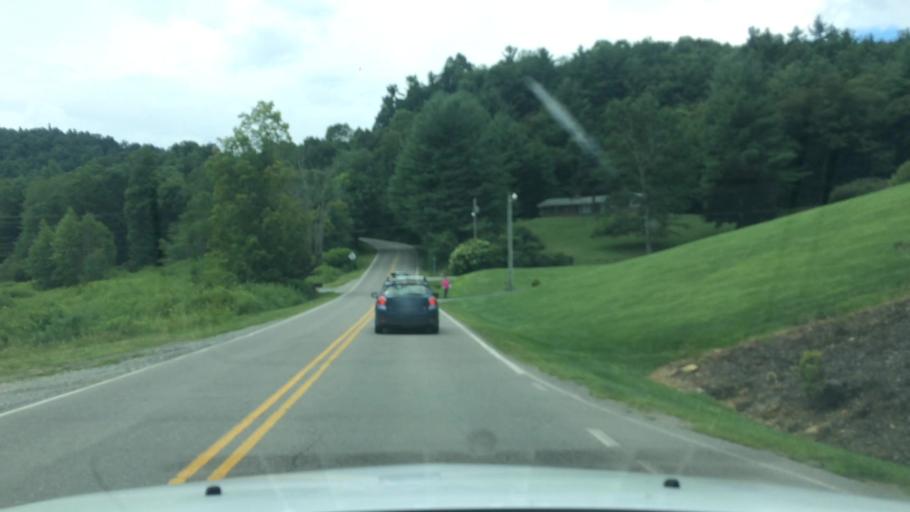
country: US
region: North Carolina
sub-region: Watauga County
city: Boone
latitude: 36.2097
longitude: -81.6302
